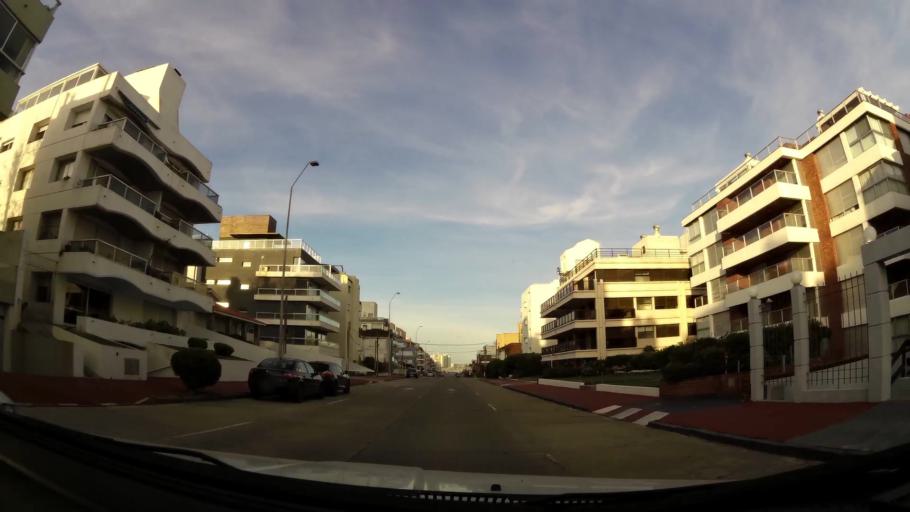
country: UY
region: Maldonado
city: Punta del Este
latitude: -34.9651
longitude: -54.9434
